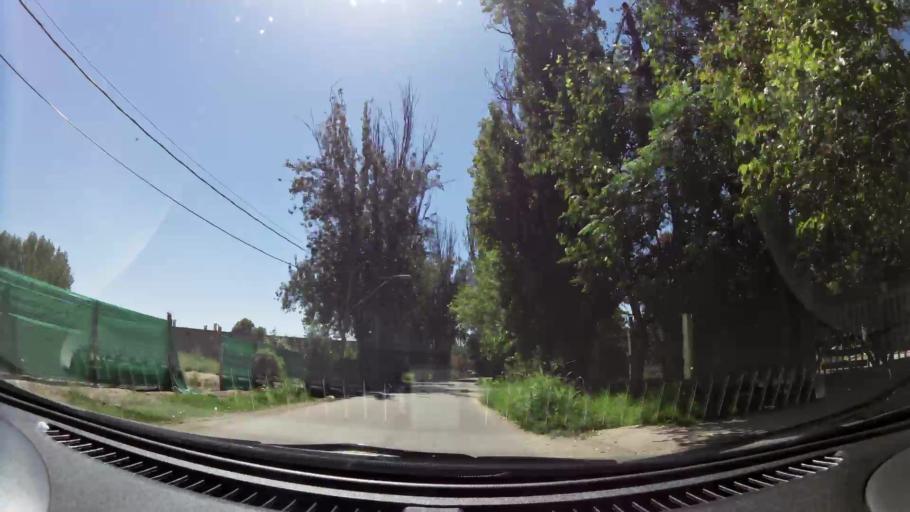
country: AR
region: Mendoza
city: Las Heras
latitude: -32.8692
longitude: -68.8004
